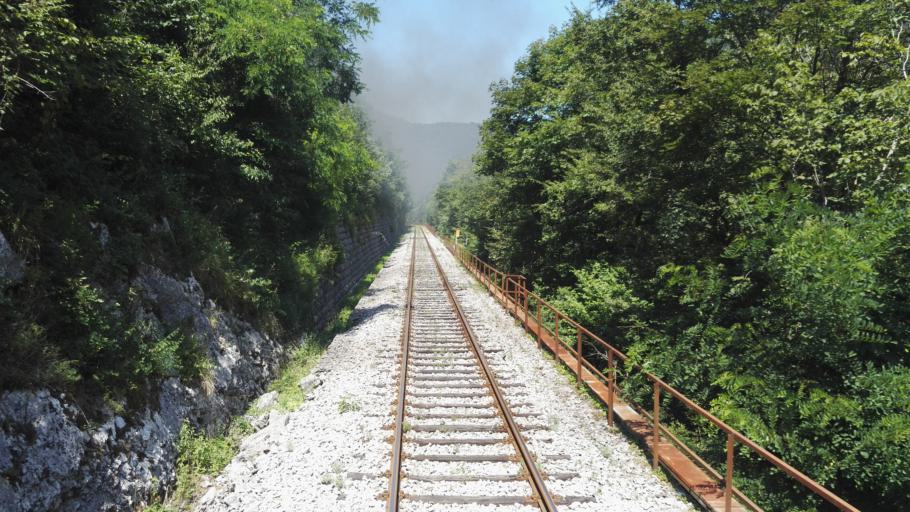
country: IT
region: Friuli Venezia Giulia
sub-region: Provincia di Gorizia
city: San Floriano del Collio
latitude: 46.0074
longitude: 13.6211
